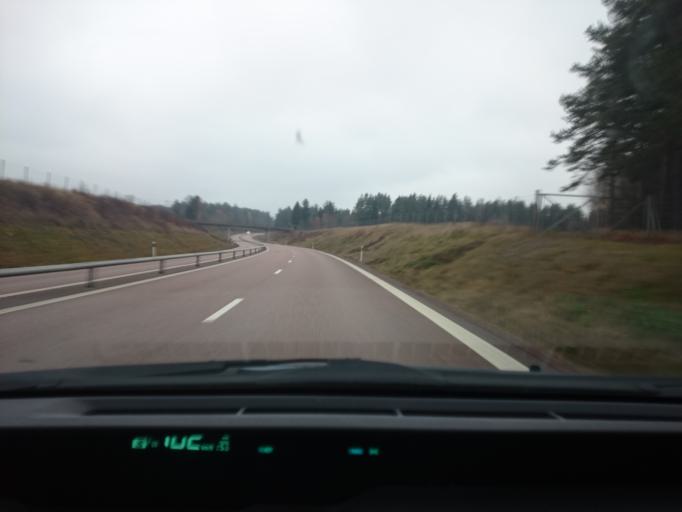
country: SE
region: Dalarna
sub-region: Saters Kommun
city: Saeter
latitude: 60.3353
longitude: 15.8186
